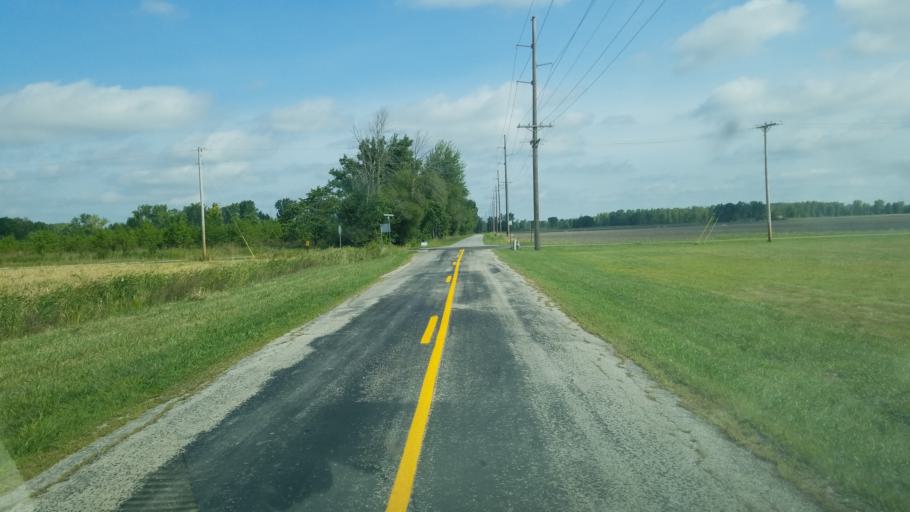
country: US
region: Ohio
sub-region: Wyandot County
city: Upper Sandusky
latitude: 40.6866
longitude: -83.3241
